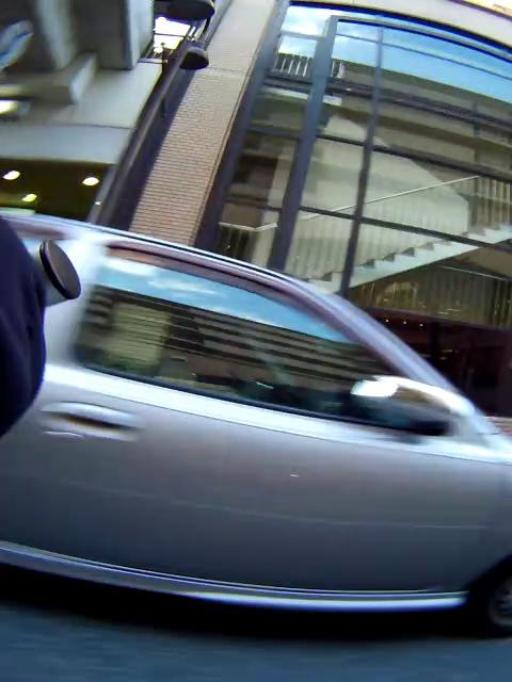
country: JP
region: Hyogo
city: Takarazuka
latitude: 34.7979
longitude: 135.3518
